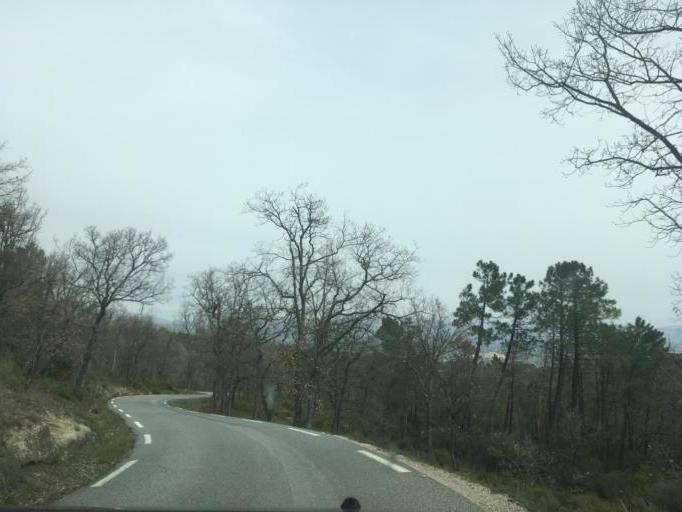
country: FR
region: Provence-Alpes-Cote d'Azur
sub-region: Departement du Var
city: Saint-Paul-en-Foret
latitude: 43.5784
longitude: 6.7266
